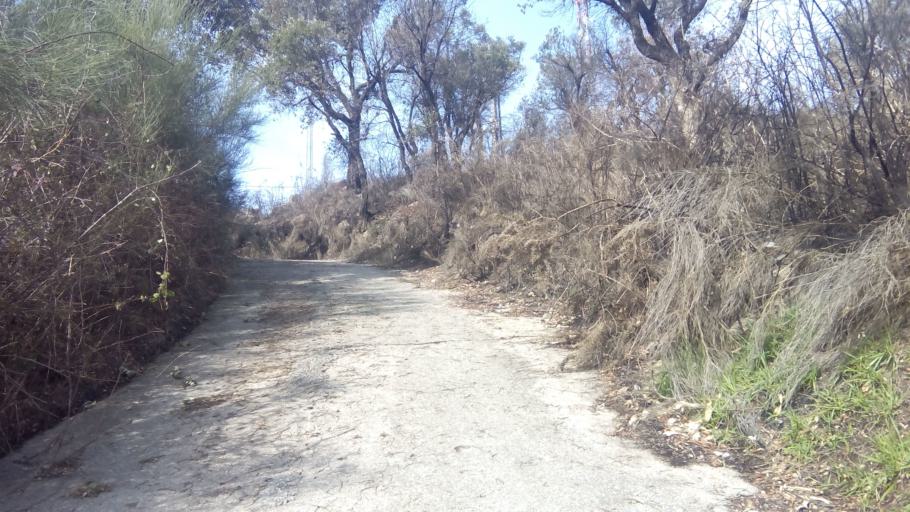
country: PT
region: Porto
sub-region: Paredes
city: Baltar
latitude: 41.1996
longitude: -8.3900
